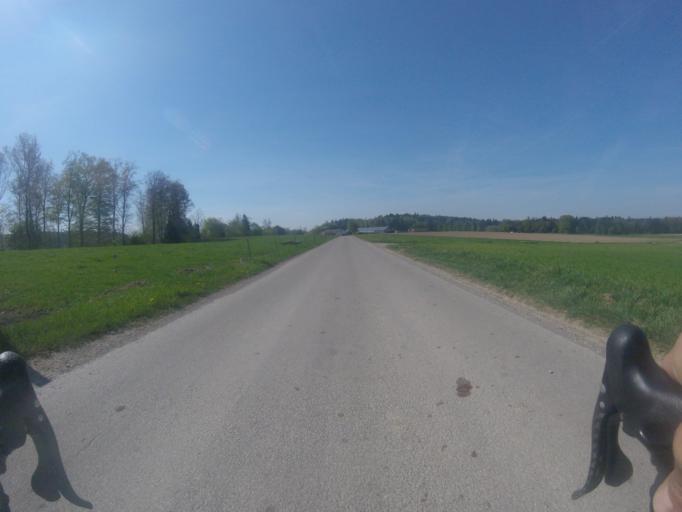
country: CH
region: Bern
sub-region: Bern-Mittelland District
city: Muhleberg
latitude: 46.9617
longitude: 7.2373
